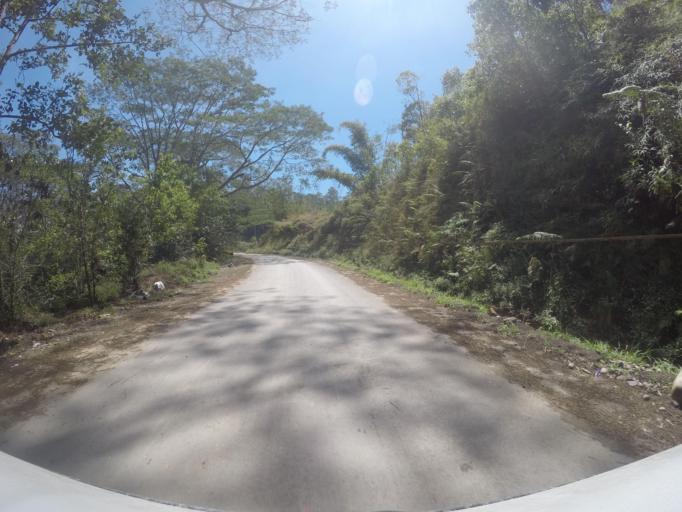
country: TL
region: Ermera
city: Gleno
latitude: -8.7878
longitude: 125.3786
